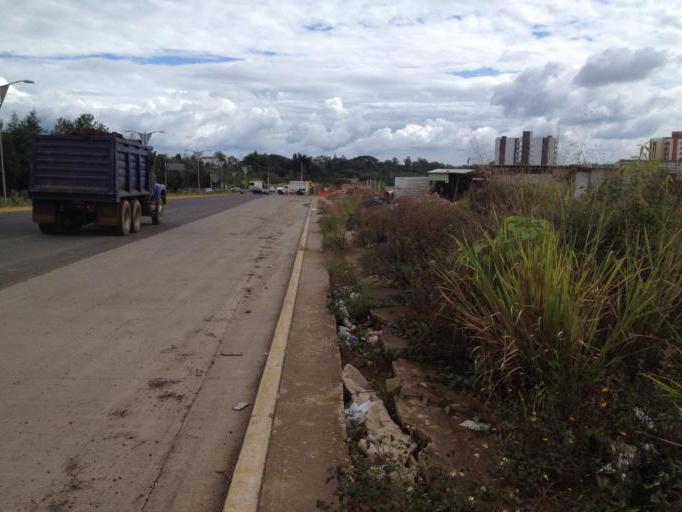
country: MX
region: Veracruz
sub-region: Emiliano Zapata
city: Las Trancas
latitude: 19.5047
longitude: -96.8591
